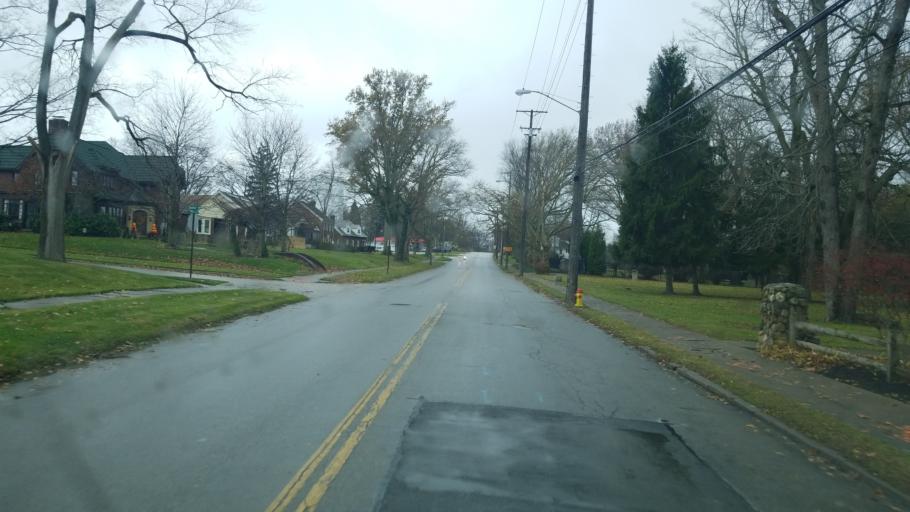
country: US
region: Ohio
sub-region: Ashtabula County
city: Ashtabula
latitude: 41.8493
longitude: -80.7969
